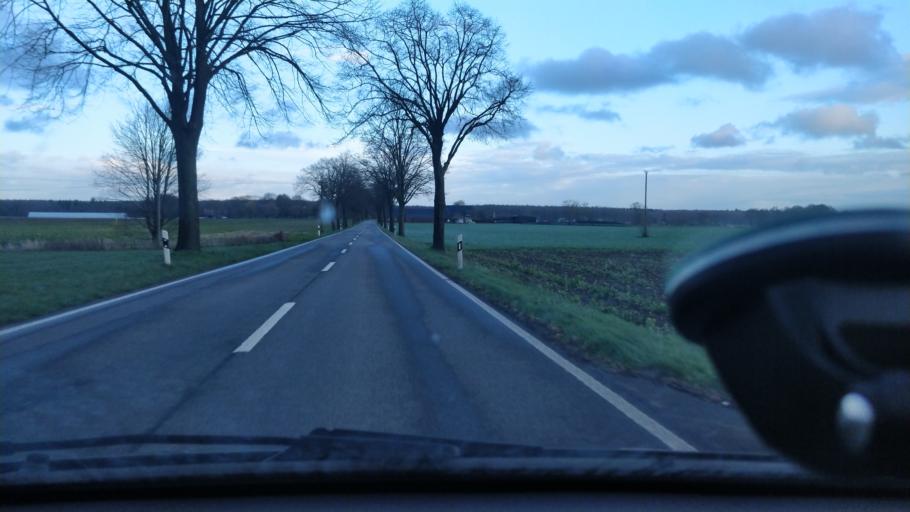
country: DE
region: North Rhine-Westphalia
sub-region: Regierungsbezirk Dusseldorf
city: Uedem
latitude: 51.6849
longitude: 6.3227
